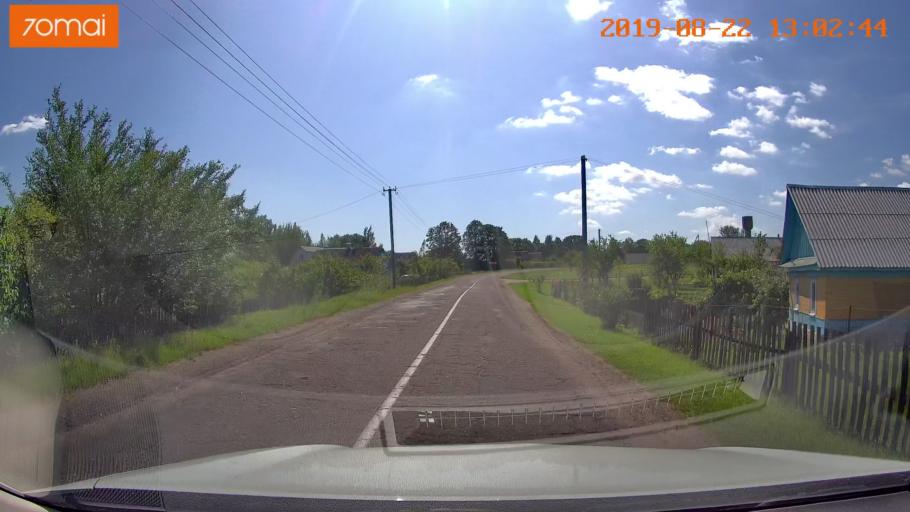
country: BY
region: Minsk
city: Prawdzinski
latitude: 53.3861
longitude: 27.8252
